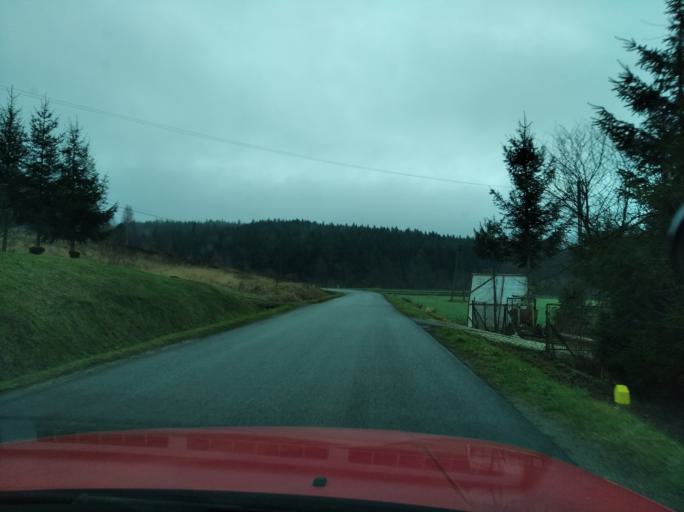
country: PL
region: Subcarpathian Voivodeship
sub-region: Powiat przemyski
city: Nienadowa
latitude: 49.8563
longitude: 22.4252
